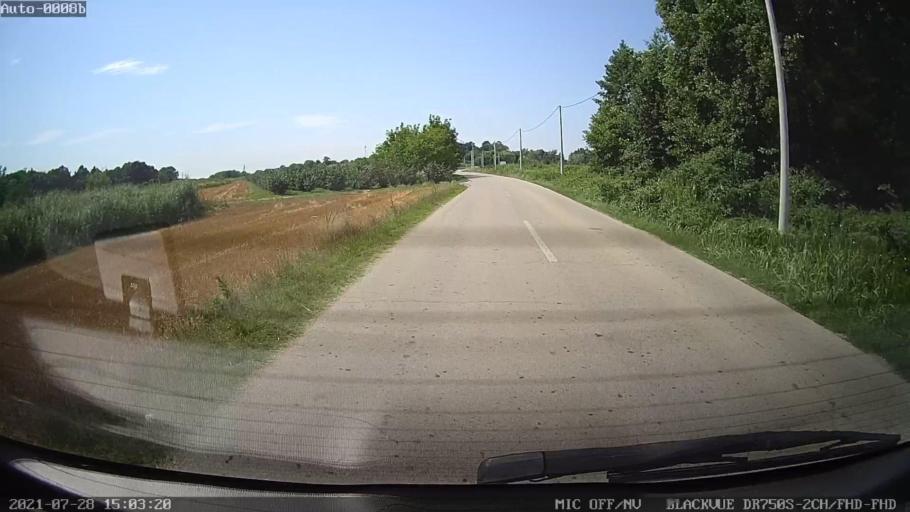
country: HR
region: Medimurska
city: Kursanec
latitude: 46.2798
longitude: 16.4190
